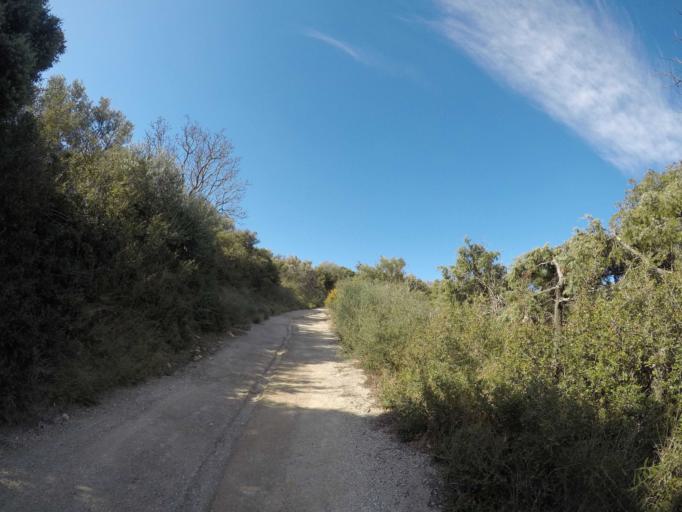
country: FR
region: Languedoc-Roussillon
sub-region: Departement des Pyrenees-Orientales
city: Millas
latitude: 42.7127
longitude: 2.6937
